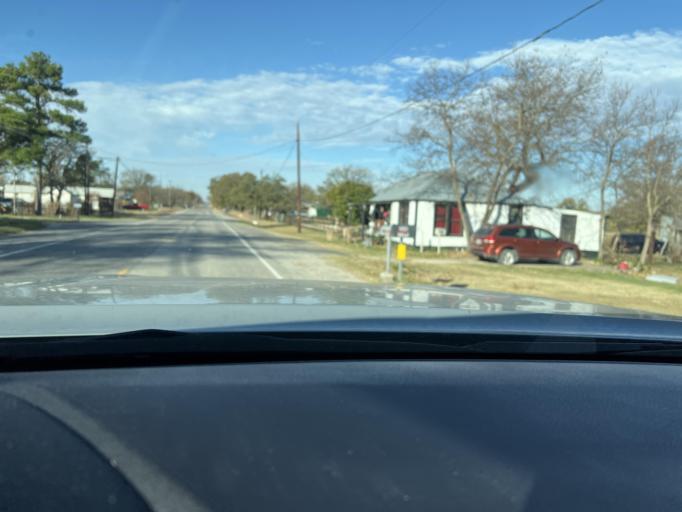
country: US
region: Texas
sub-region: Eastland County
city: Eastland
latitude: 32.4193
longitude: -98.7454
